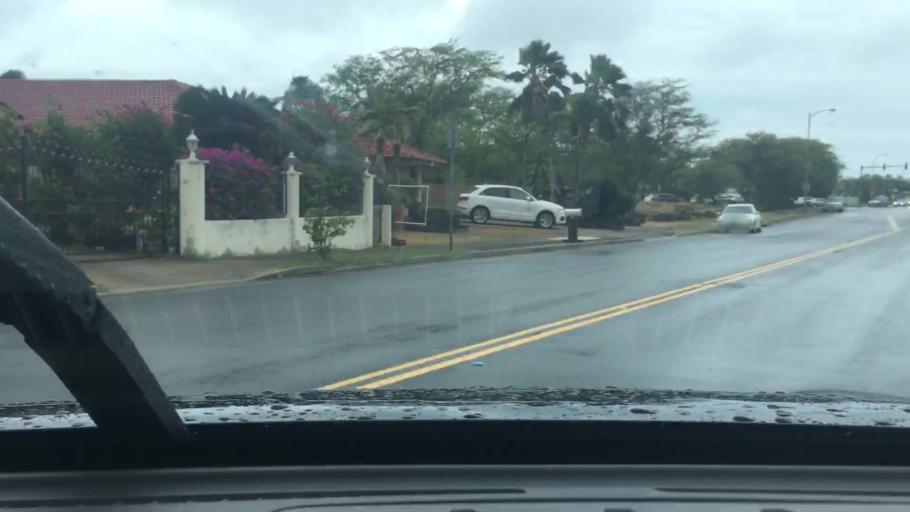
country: US
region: Hawaii
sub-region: Honolulu County
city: Waimanalo Beach
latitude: 21.2895
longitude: -157.7012
